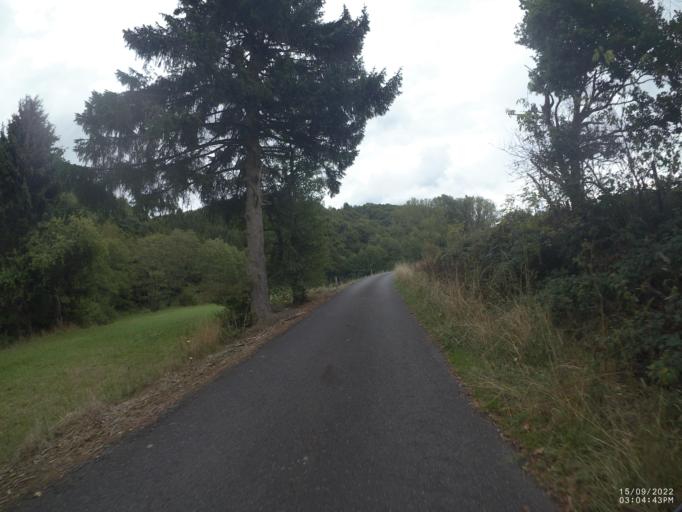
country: DE
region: Rheinland-Pfalz
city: Bongard
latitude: 50.2959
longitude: 6.8111
